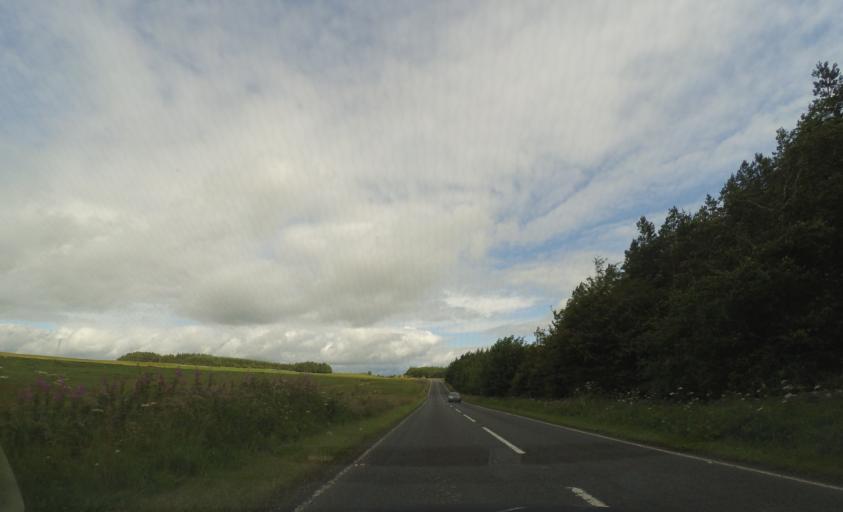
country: GB
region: Scotland
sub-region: The Scottish Borders
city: Hawick
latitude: 55.4675
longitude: -2.7903
